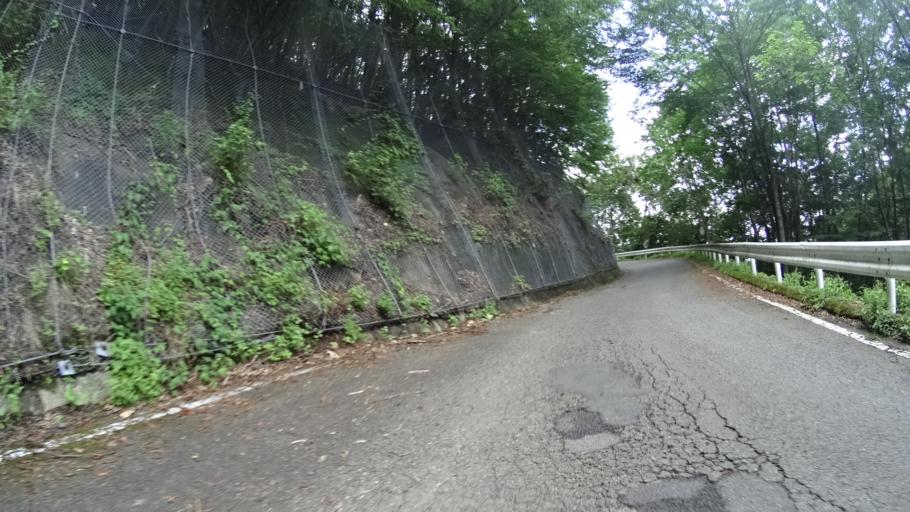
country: JP
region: Nagano
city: Saku
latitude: 36.0662
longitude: 138.6546
